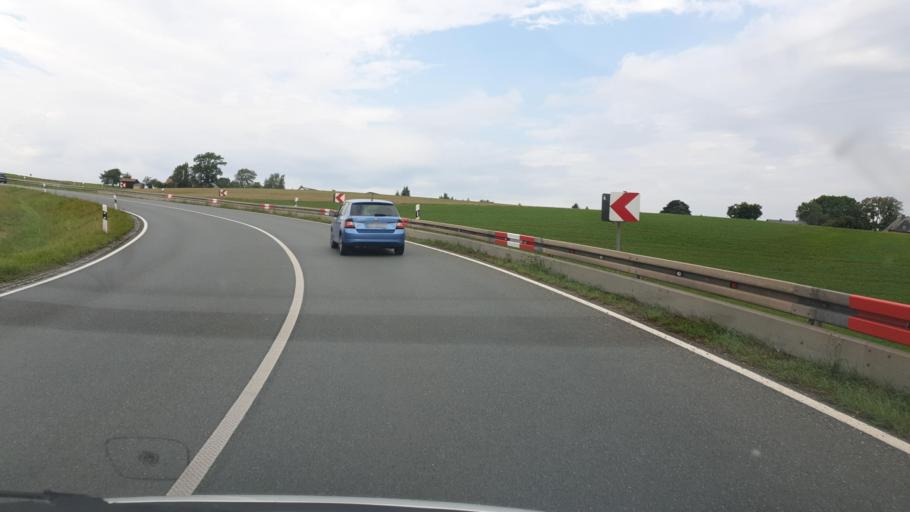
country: DE
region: Saxony
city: Lengenfeld
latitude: 50.5838
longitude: 12.3525
